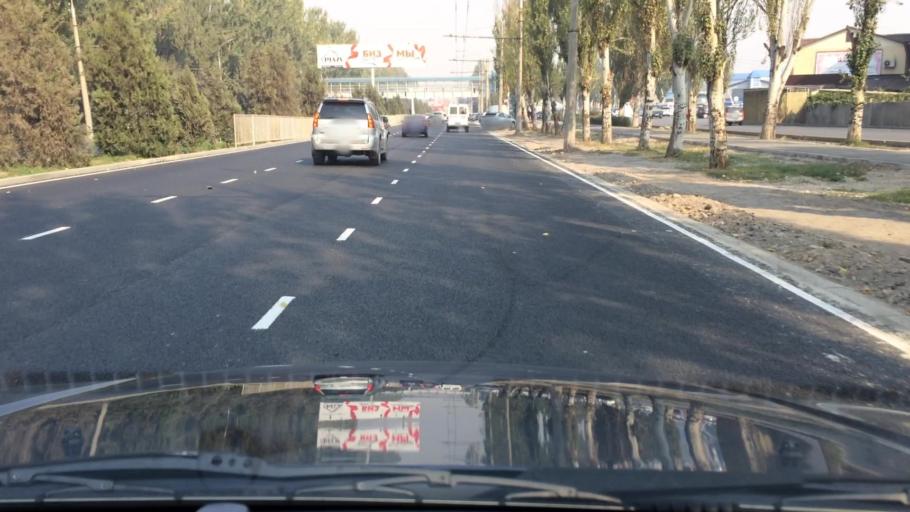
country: KG
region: Chuy
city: Lebedinovka
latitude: 42.8698
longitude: 74.6368
